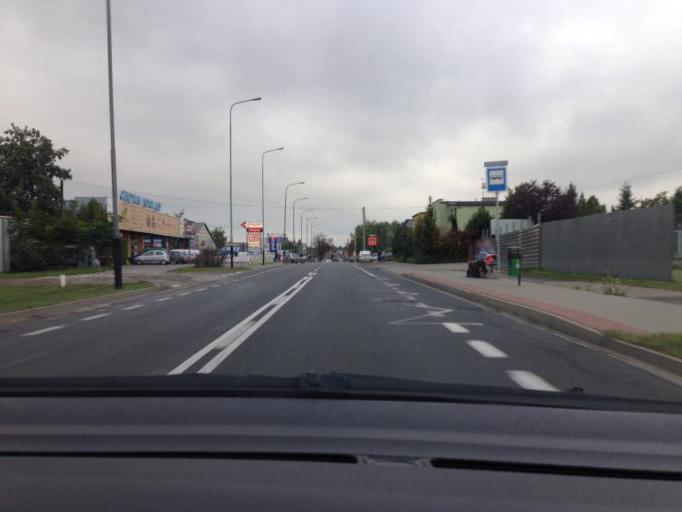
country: PL
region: Greater Poland Voivodeship
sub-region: Powiat poznanski
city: Suchy Las
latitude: 52.4484
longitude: 16.8961
